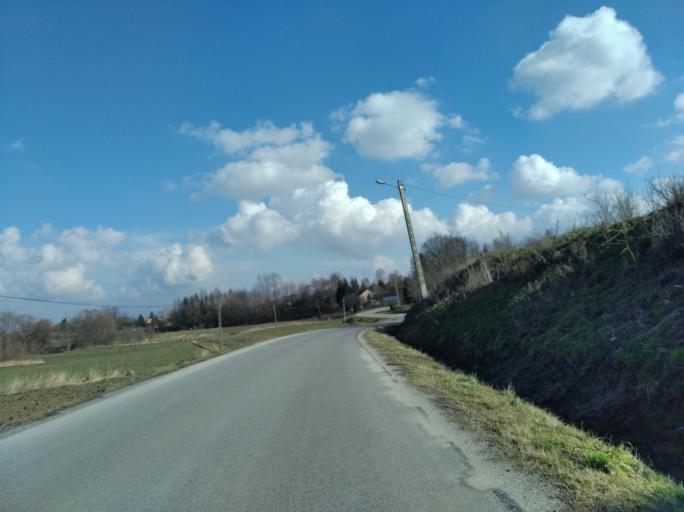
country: PL
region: Subcarpathian Voivodeship
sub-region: Powiat strzyzowski
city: Wisniowa
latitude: 49.8582
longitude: 21.6508
